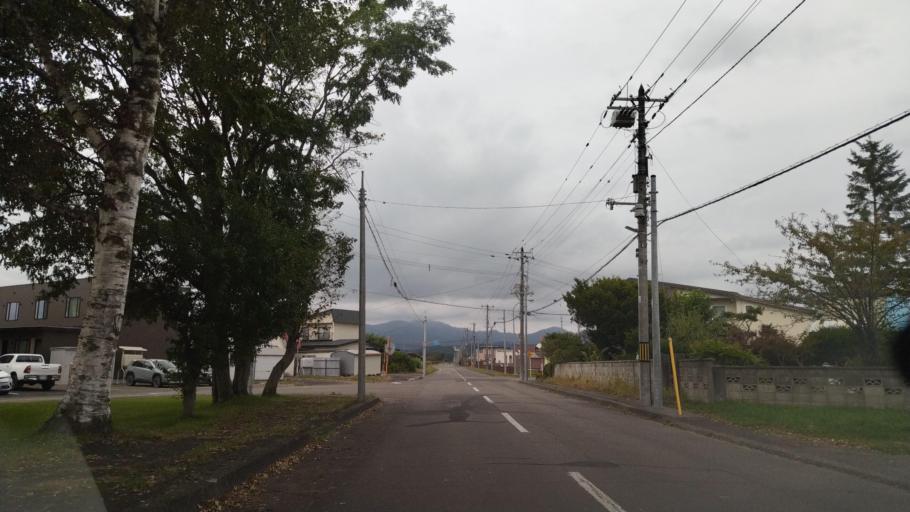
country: JP
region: Hokkaido
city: Otofuke
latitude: 43.2339
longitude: 143.2887
